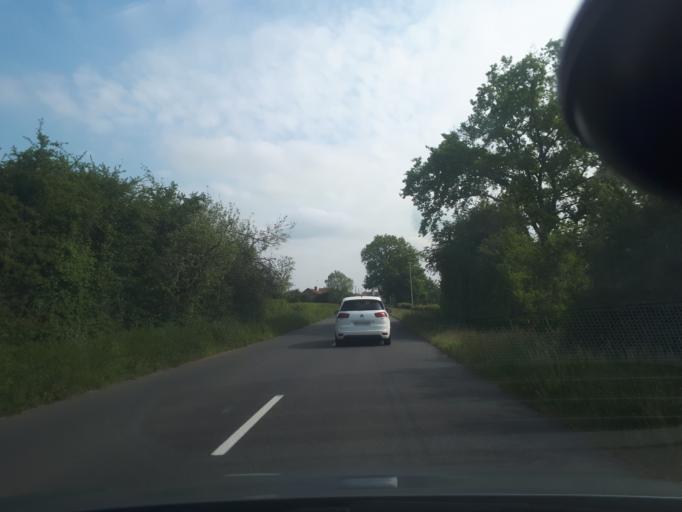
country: FR
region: Auvergne
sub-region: Departement de l'Allier
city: Dompierre-sur-Besbre
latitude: 46.4405
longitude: 3.6267
